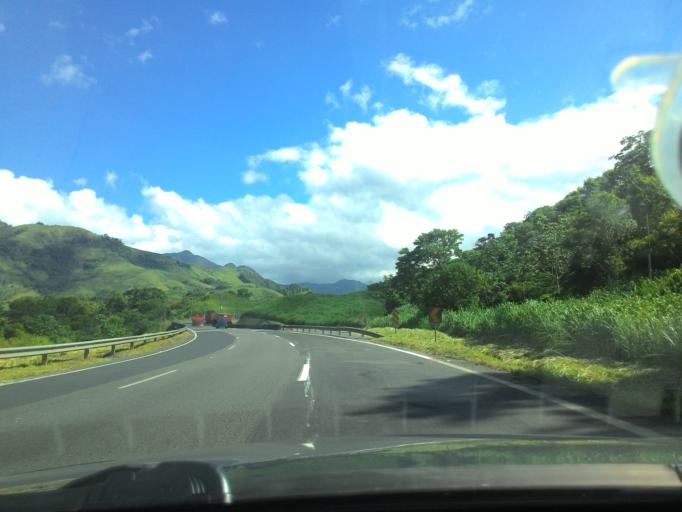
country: BR
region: Sao Paulo
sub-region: Cajati
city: Cajati
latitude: -24.8194
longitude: -48.2148
